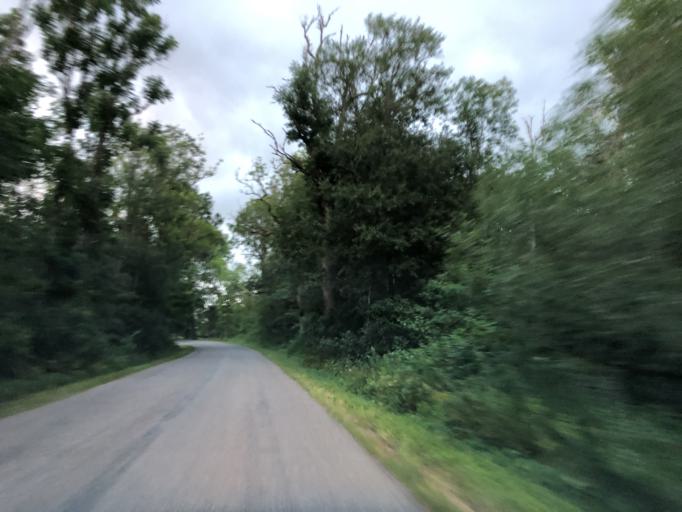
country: EE
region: Laeaene
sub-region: Ridala Parish
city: Uuemoisa
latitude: 58.9048
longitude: 23.6919
